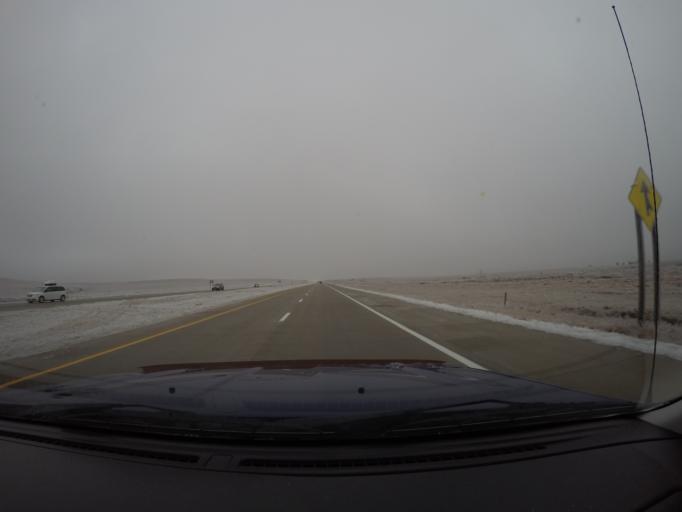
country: US
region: Kansas
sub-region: Wabaunsee County
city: Alma
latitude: 39.0656
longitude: -96.3835
